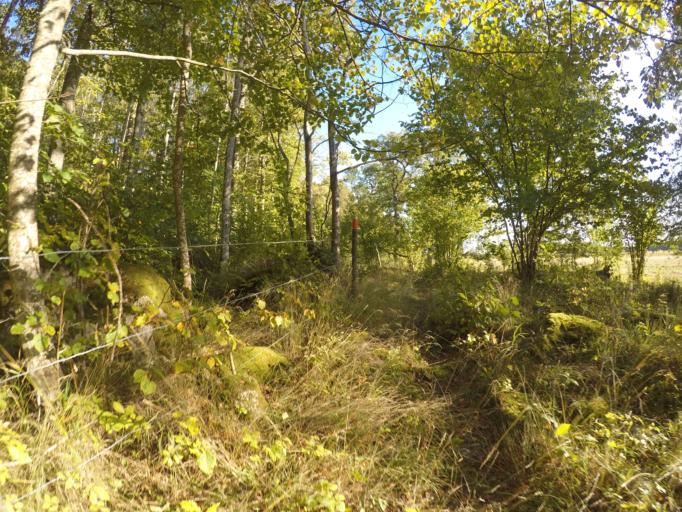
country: SE
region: Vaestmanland
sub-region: Hallstahammars Kommun
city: Kolback
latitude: 59.4767
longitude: 16.2264
